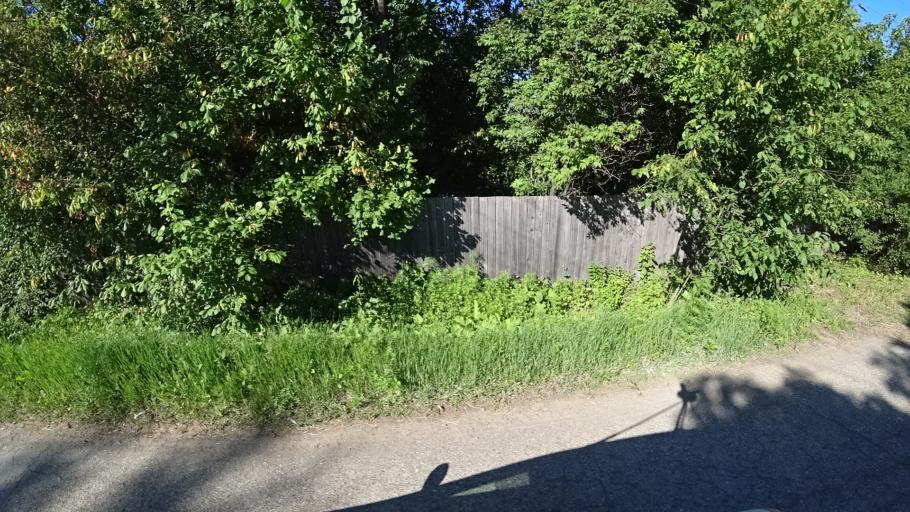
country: RU
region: Khabarovsk Krai
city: Khor
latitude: 47.8869
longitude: 134.9939
